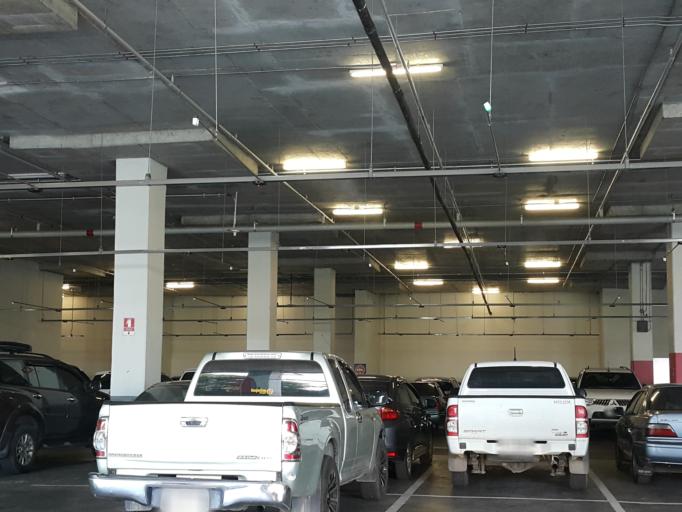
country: TH
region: Chiang Mai
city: Chiang Mai
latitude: 18.8082
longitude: 99.0189
